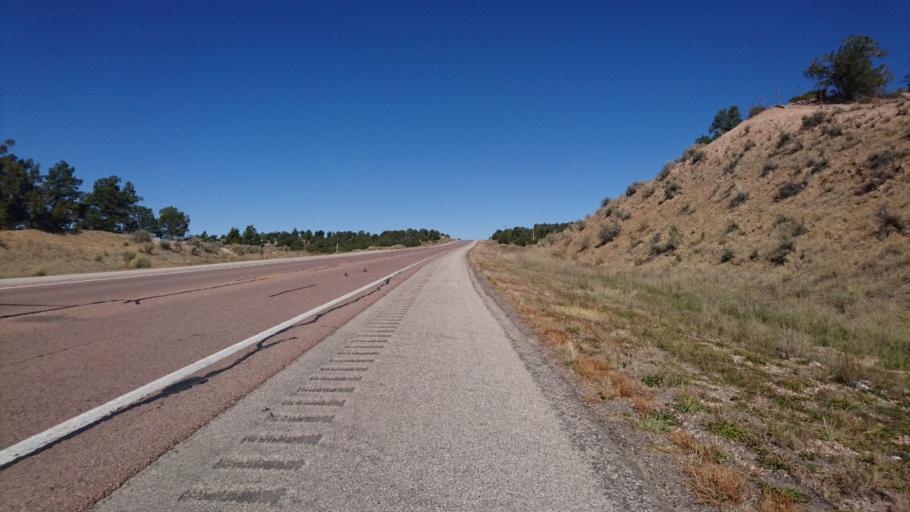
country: US
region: New Mexico
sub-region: McKinley County
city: Black Rock
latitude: 35.3036
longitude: -108.7575
